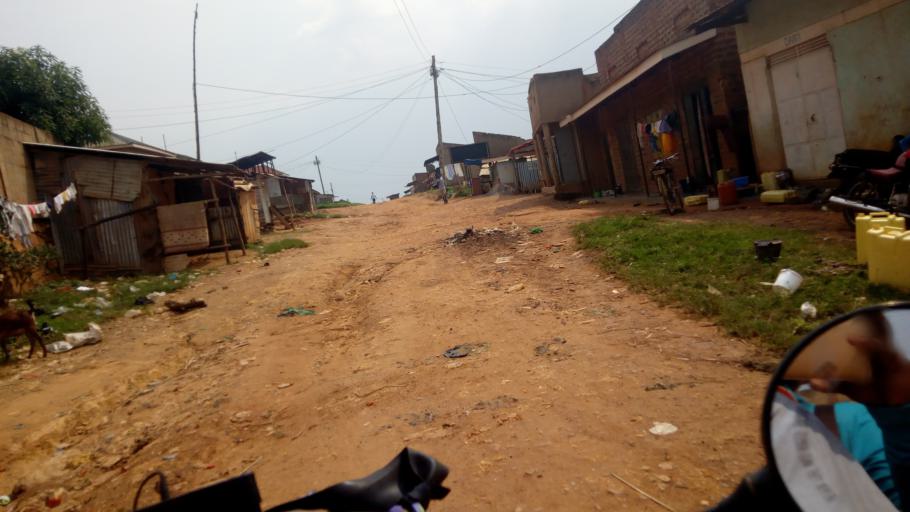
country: UG
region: Central Region
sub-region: Wakiso District
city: Kireka
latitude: 0.3251
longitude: 32.6550
